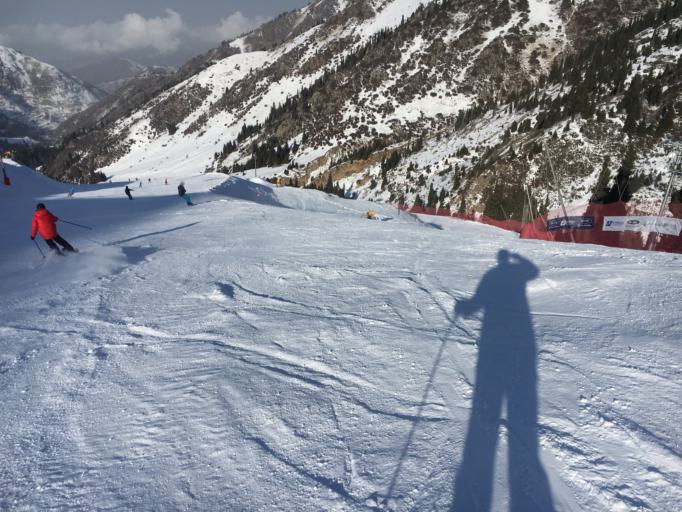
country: KZ
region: Almaty Qalasy
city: Almaty
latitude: 43.1212
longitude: 77.0954
